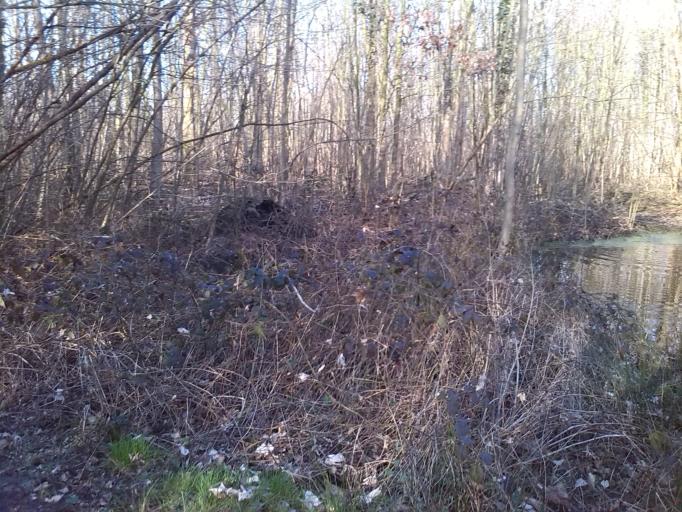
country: BE
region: Flanders
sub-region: Provincie West-Vlaanderen
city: Brugge
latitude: 51.2373
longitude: 3.2100
